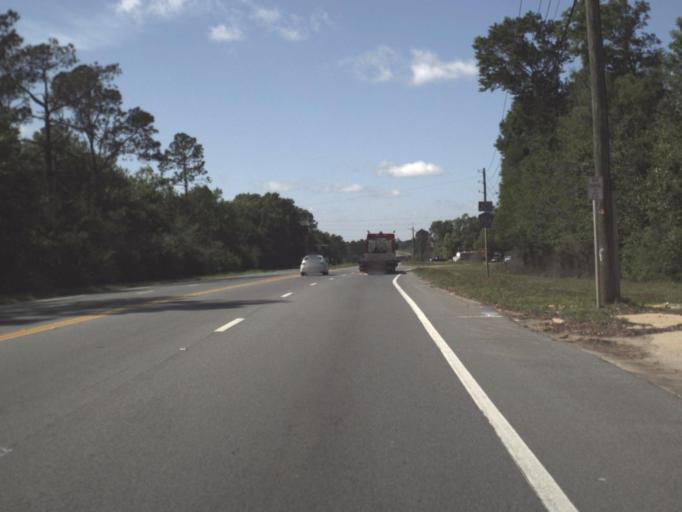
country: US
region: Florida
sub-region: Escambia County
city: Cantonment
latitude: 30.6133
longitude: -87.3216
